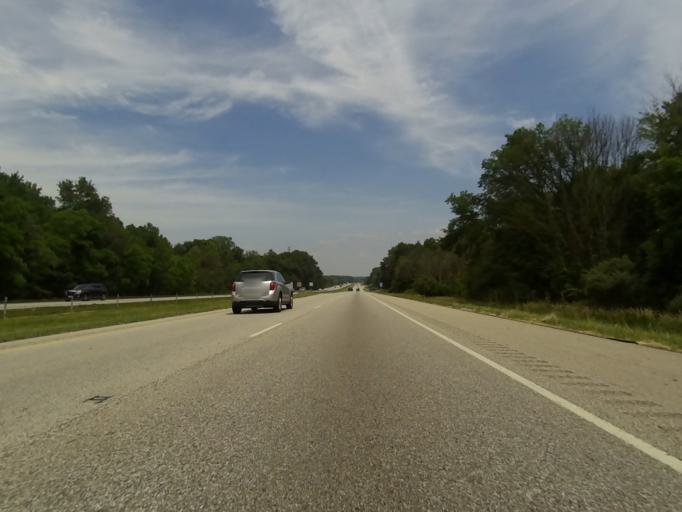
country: US
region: Ohio
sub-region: Mahoning County
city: Craig Beach
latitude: 41.1059
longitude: -81.0637
